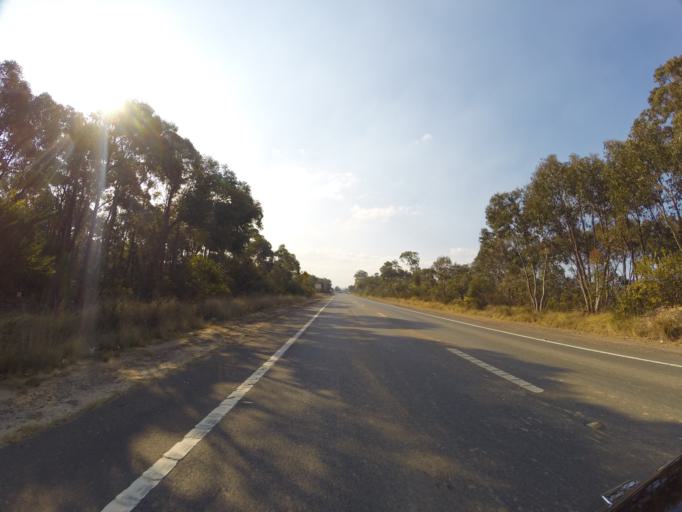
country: AU
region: New South Wales
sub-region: Sutherland Shire
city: Menai
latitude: -33.9959
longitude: 150.9964
